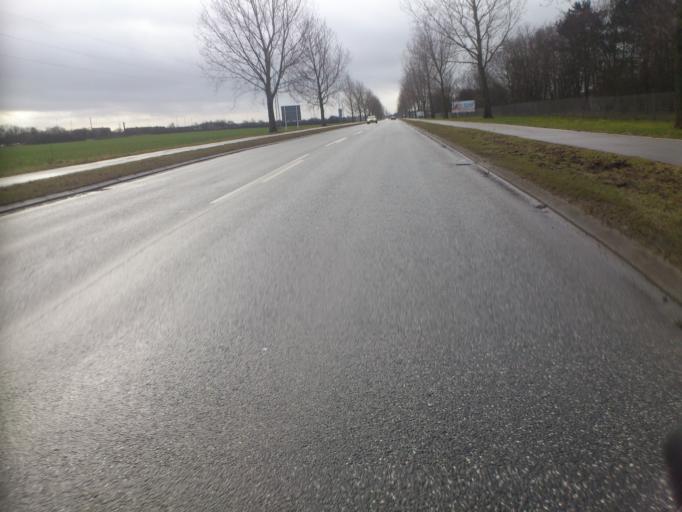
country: DK
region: South Denmark
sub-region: Fredericia Kommune
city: Fredericia
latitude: 55.5996
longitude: 9.7575
